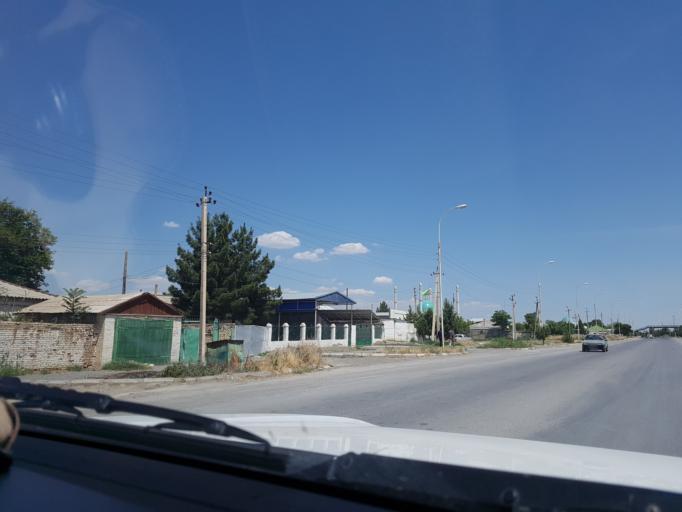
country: TM
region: Ahal
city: Abadan
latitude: 38.1632
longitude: 57.9596
